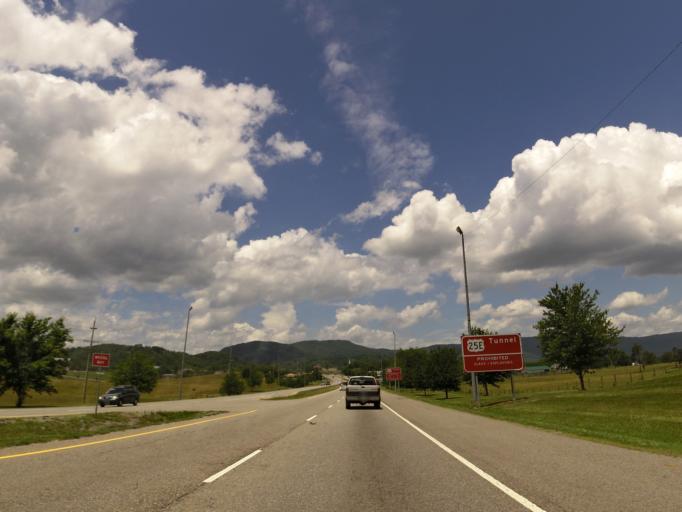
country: US
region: Tennessee
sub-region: Claiborne County
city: Harrogate
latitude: 36.5683
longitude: -83.6534
